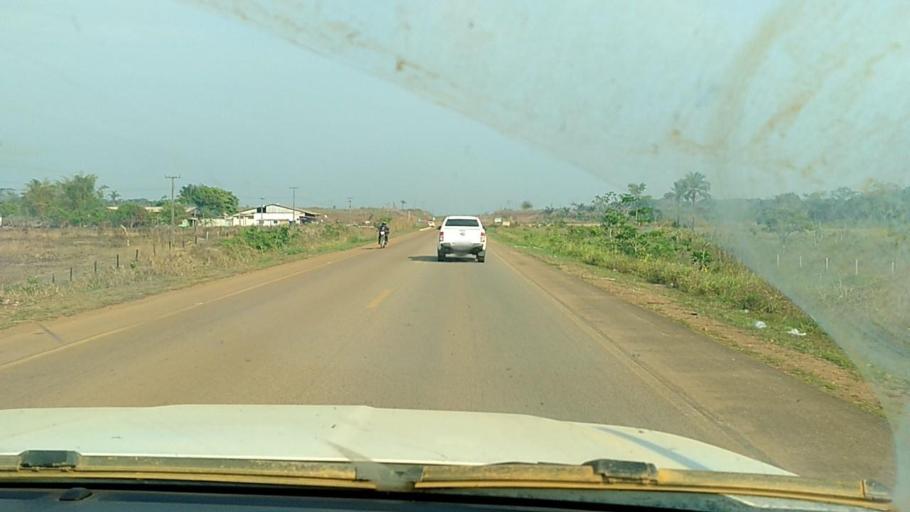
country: BR
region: Rondonia
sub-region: Porto Velho
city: Porto Velho
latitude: -8.7358
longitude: -63.9614
